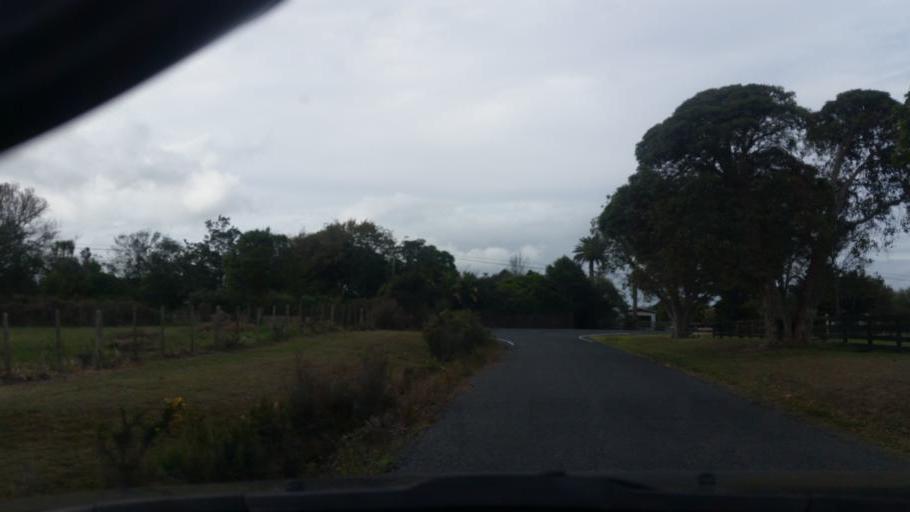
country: NZ
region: Northland
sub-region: Kaipara District
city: Dargaville
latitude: -36.0269
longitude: 173.9160
